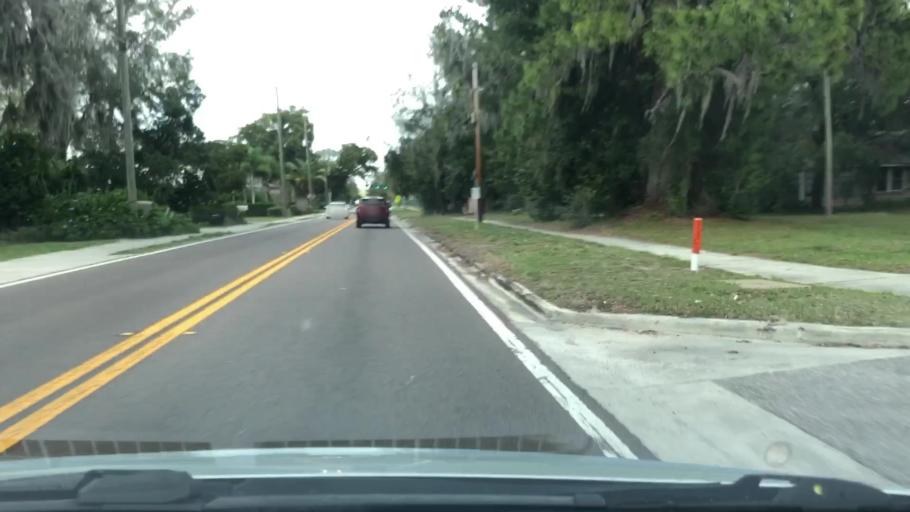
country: US
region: Florida
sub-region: Seminole County
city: Forest City
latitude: 28.6505
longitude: -81.4438
